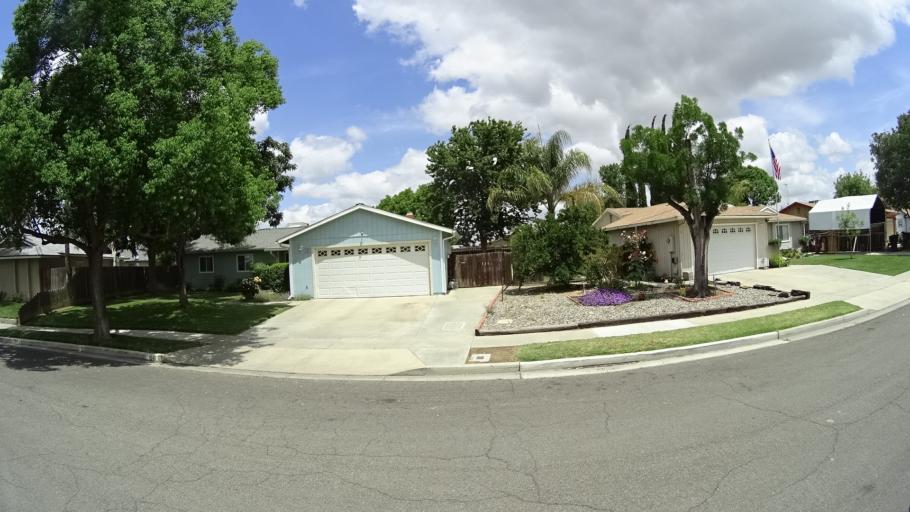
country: US
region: California
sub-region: Kings County
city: Hanford
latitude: 36.3115
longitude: -119.6701
